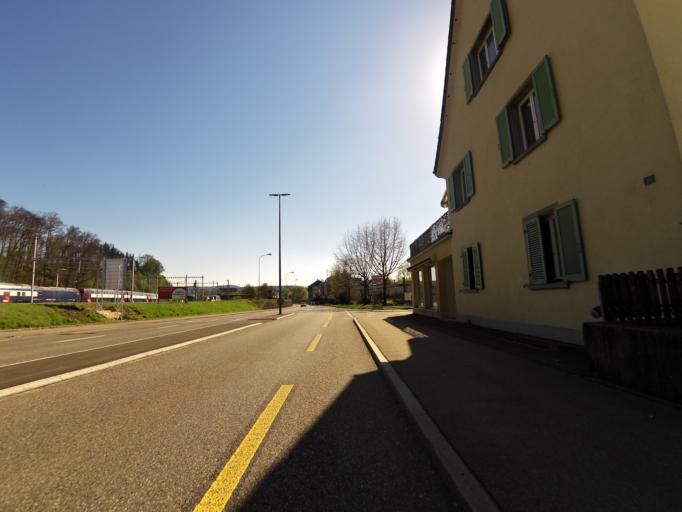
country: CH
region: Aargau
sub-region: Bezirk Zurzach
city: Koblenz
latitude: 47.6029
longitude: 8.2282
